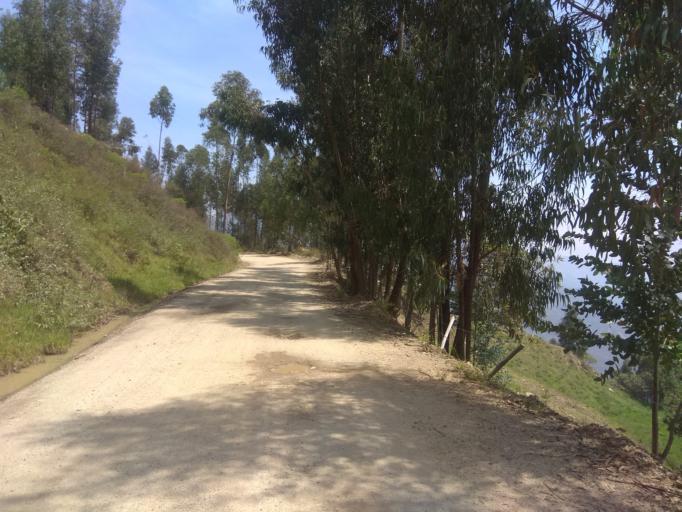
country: CO
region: Boyaca
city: Socha Viejo
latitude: 5.9788
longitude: -72.7301
